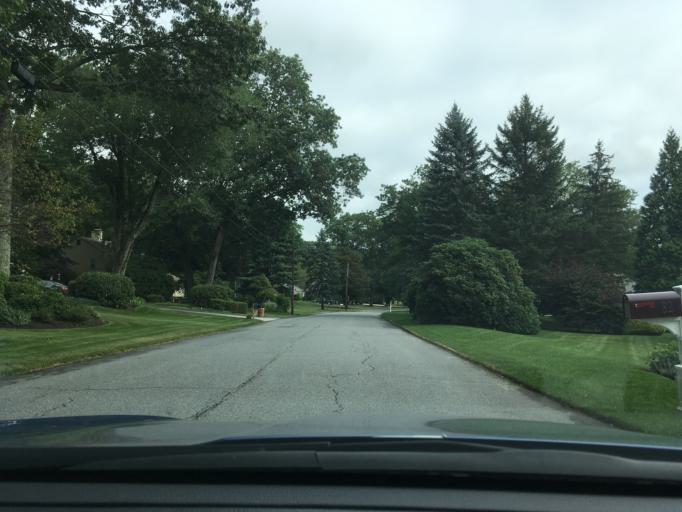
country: US
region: Rhode Island
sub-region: Kent County
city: East Greenwich
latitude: 41.6564
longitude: -71.4869
